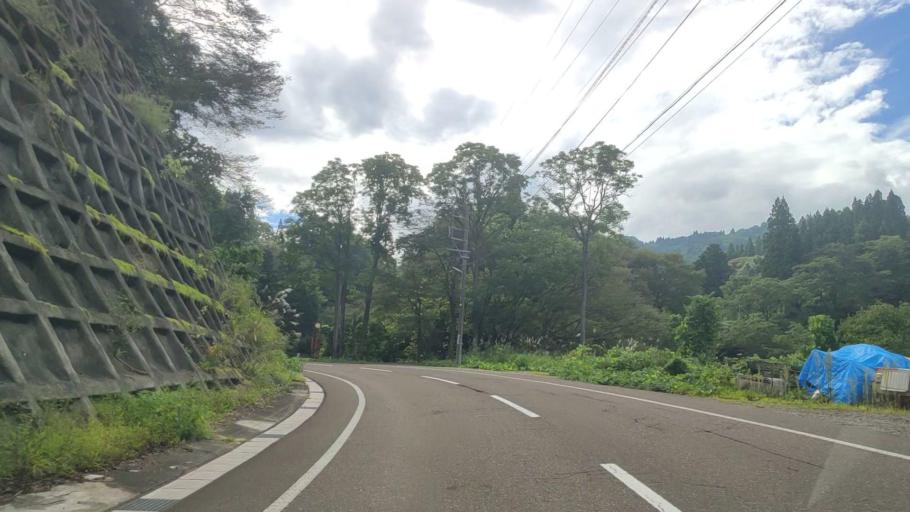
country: JP
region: Niigata
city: Arai
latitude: 36.9320
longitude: 138.2977
